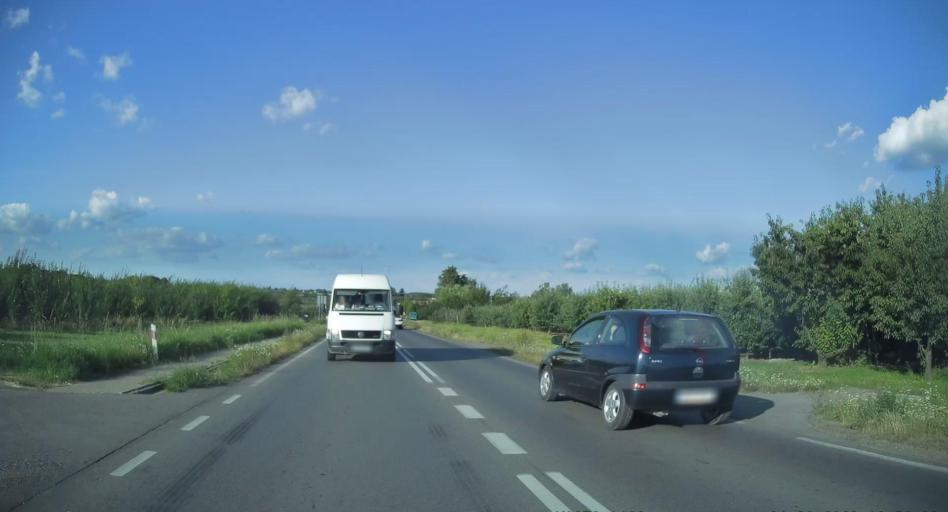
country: PL
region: Masovian Voivodeship
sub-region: Powiat grojecki
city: Belsk Duzy
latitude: 51.8410
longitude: 20.8289
